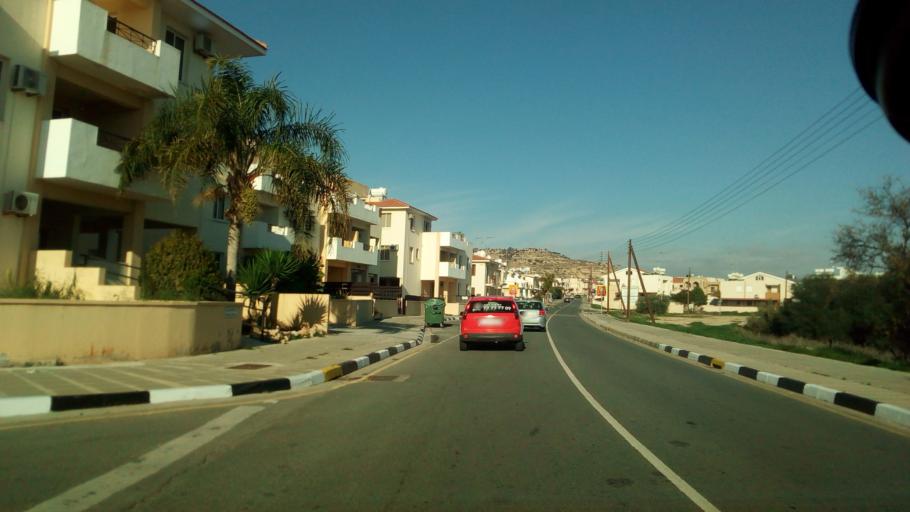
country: CY
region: Larnaka
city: Voroklini
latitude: 34.9775
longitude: 33.6623
